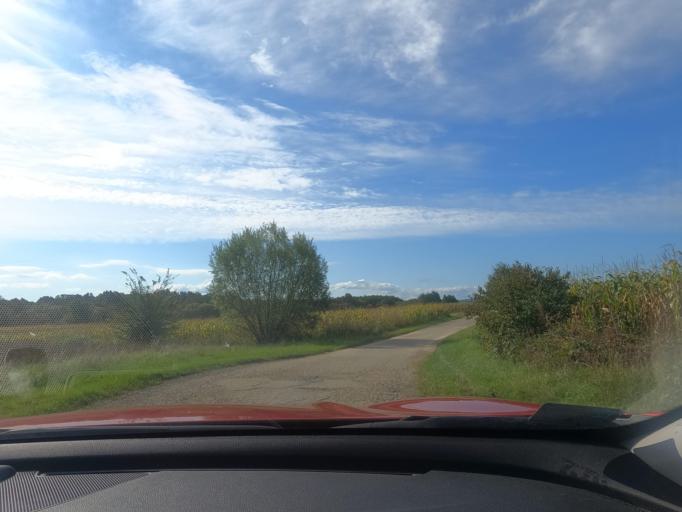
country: HR
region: Sisacko-Moslavacka
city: Petrinja
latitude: 45.3365
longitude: 16.2178
